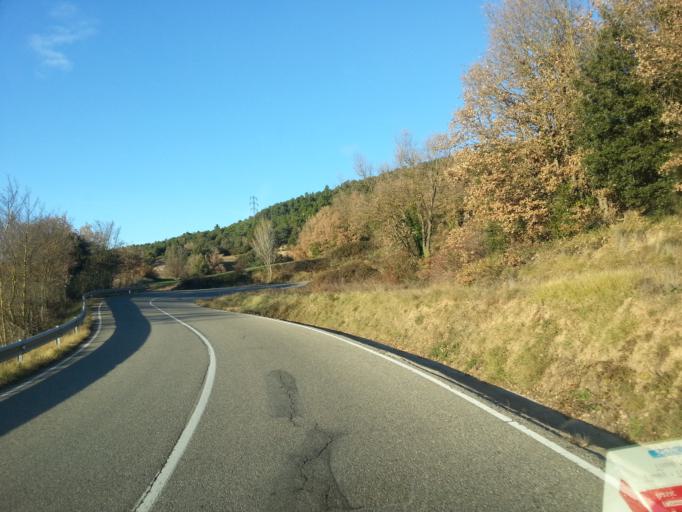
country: ES
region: Catalonia
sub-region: Provincia de Lleida
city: Solsona
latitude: 42.0502
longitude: 1.5108
